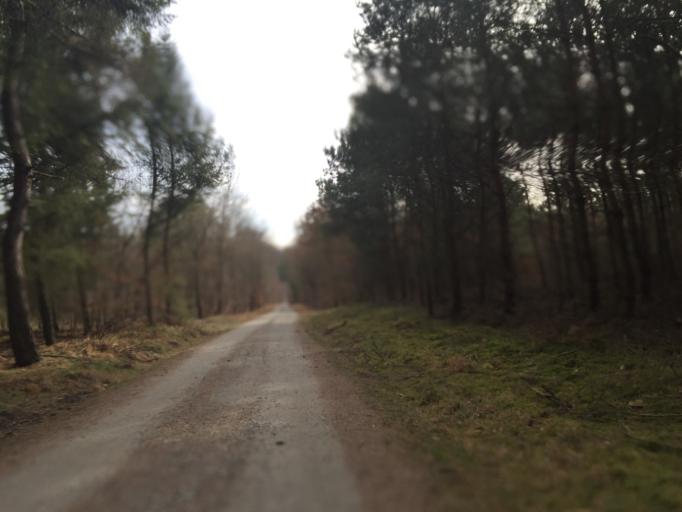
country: DE
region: Hesse
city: Viernheim
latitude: 49.5617
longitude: 8.5787
